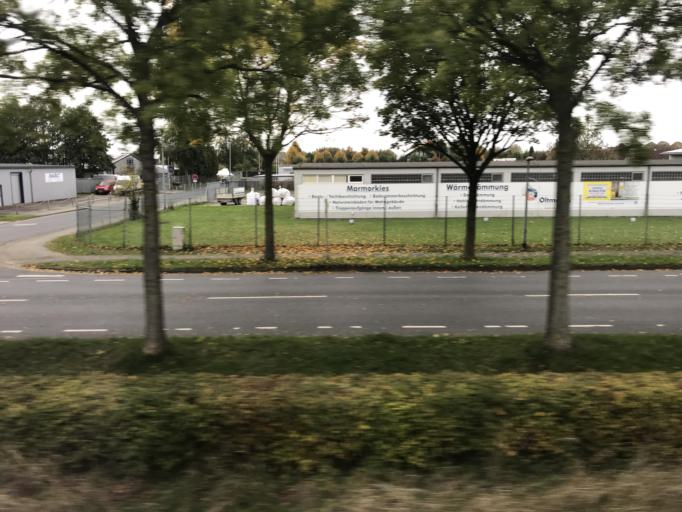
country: DE
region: Lower Saxony
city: Emden
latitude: 53.3513
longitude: 7.1915
